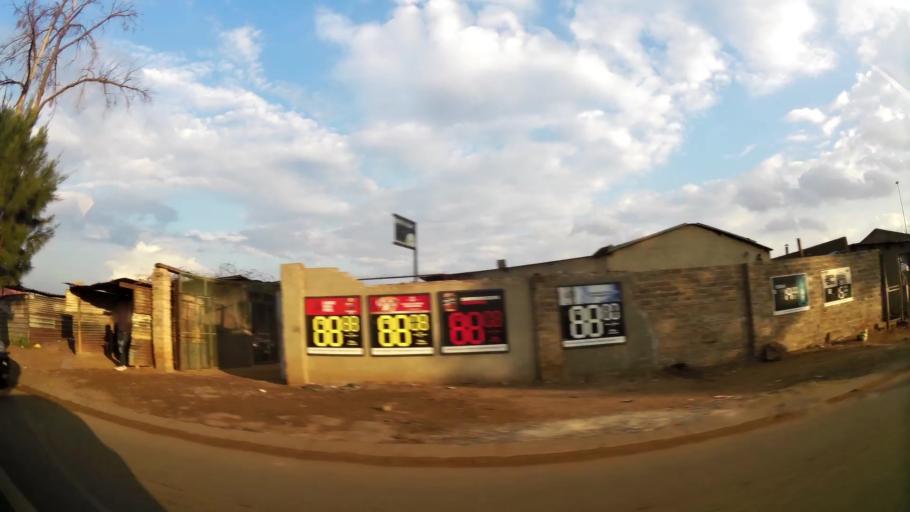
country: ZA
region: Gauteng
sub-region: City of Johannesburg Metropolitan Municipality
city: Orange Farm
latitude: -26.5938
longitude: 27.8280
